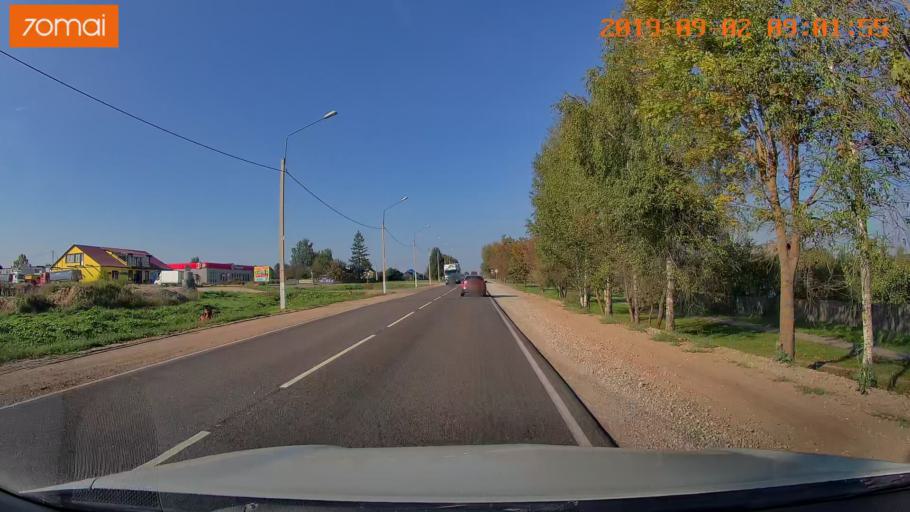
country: RU
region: Kaluga
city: Myatlevo
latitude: 54.9035
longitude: 35.6800
